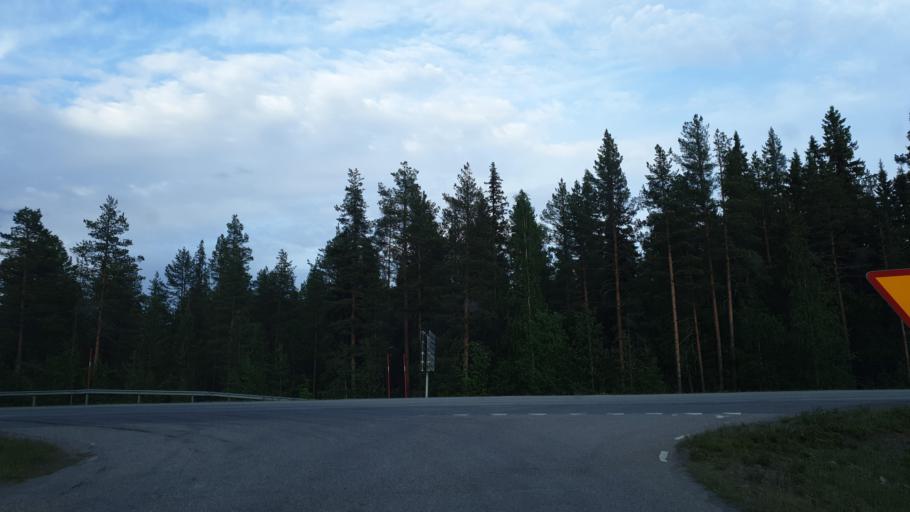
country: SE
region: Norrbotten
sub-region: Arvidsjaurs Kommun
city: Arvidsjaur
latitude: 65.9519
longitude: 19.5199
